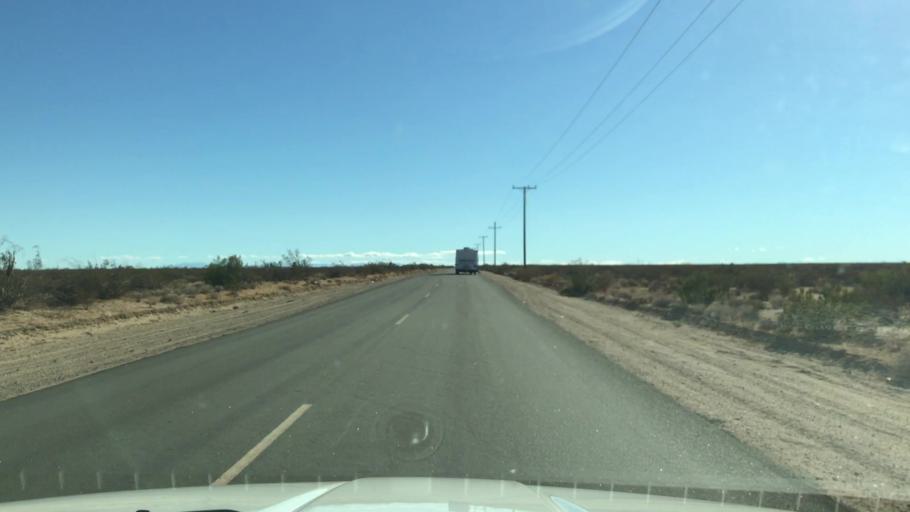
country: US
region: California
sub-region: Kern County
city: California City
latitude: 35.2313
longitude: -117.9859
